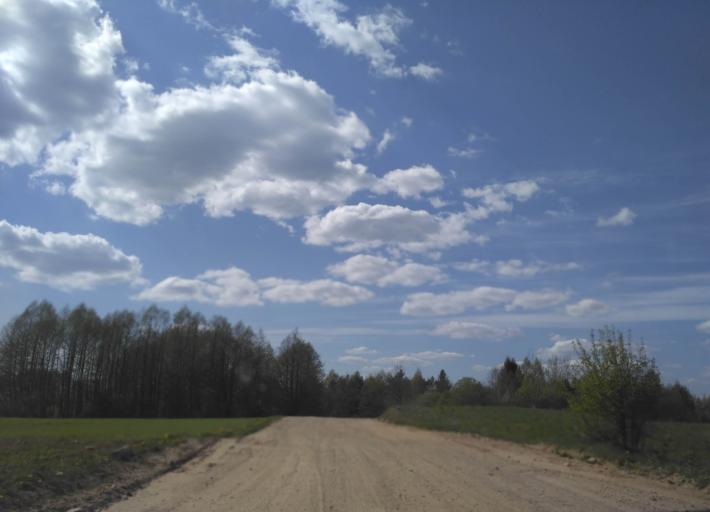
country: BY
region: Minsk
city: Narach
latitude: 54.9727
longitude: 26.6297
